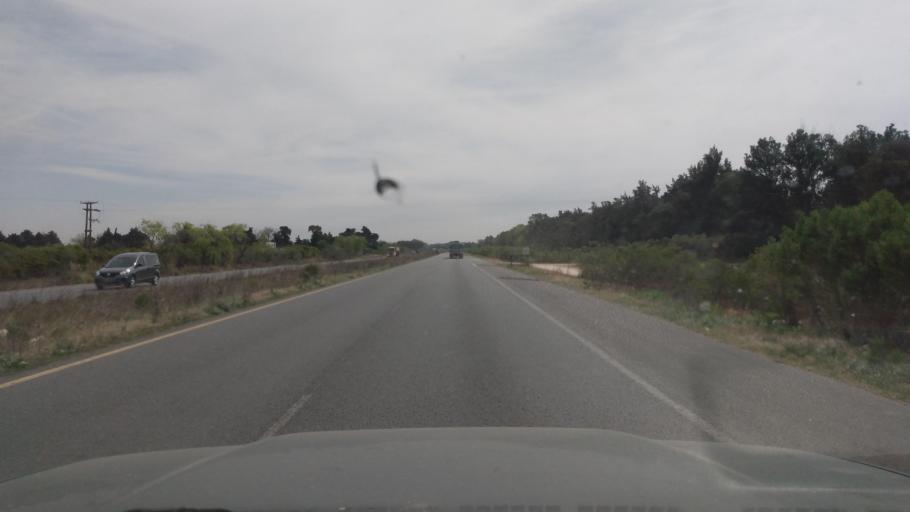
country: AR
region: Buenos Aires
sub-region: Partido de Lujan
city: Lujan
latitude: -34.5139
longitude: -59.0390
